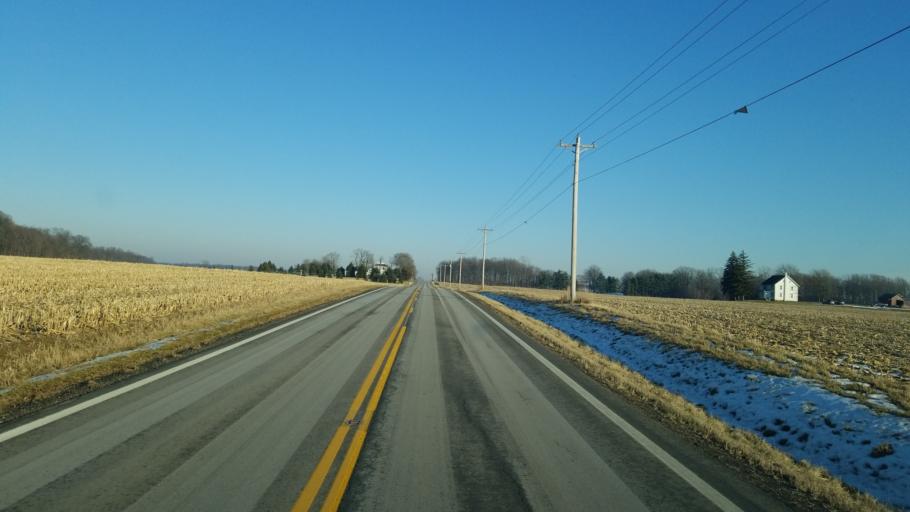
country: US
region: Ohio
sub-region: Crawford County
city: Bucyrus
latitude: 40.9649
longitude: -82.9305
